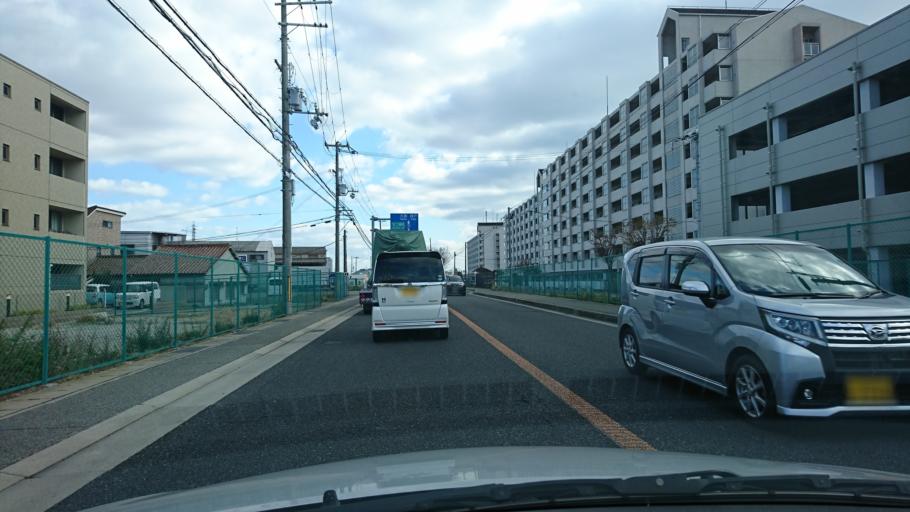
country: JP
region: Hyogo
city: Akashi
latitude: 34.6606
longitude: 134.9692
